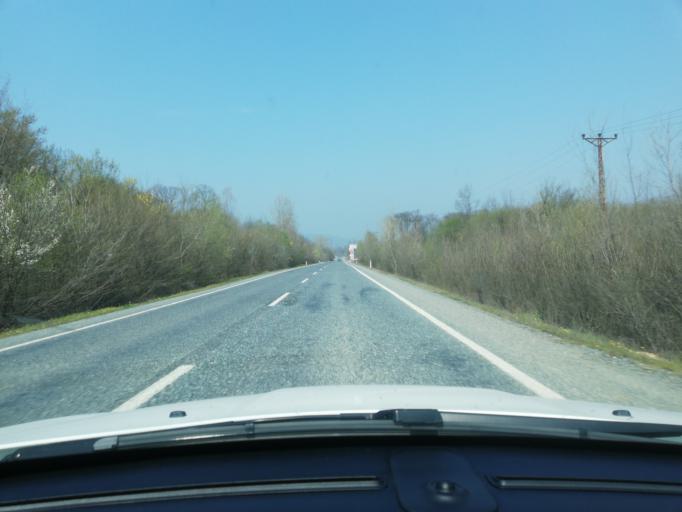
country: TR
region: Zonguldak
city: Gokcebey
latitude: 41.2932
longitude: 32.1326
